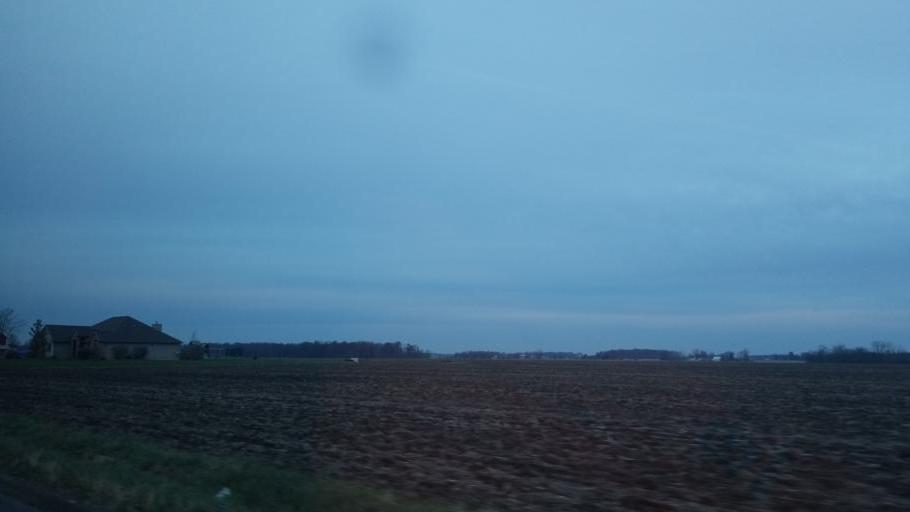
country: US
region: Indiana
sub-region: Adams County
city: Decatur
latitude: 40.7828
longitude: -85.0146
